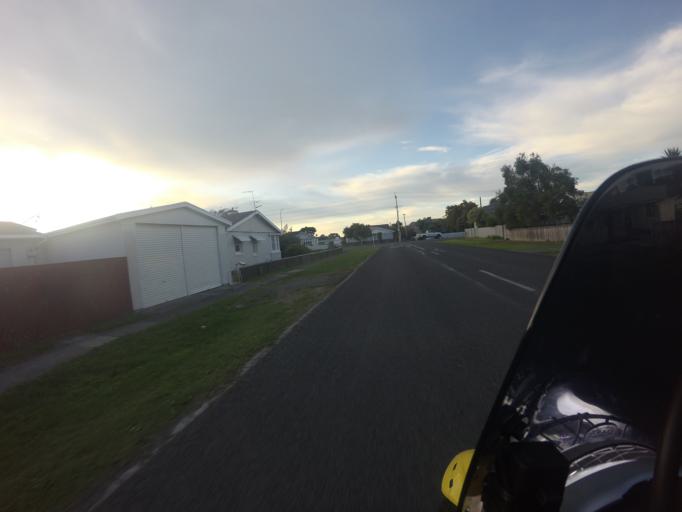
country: NZ
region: Gisborne
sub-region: Gisborne District
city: Gisborne
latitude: -38.6707
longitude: 178.0436
